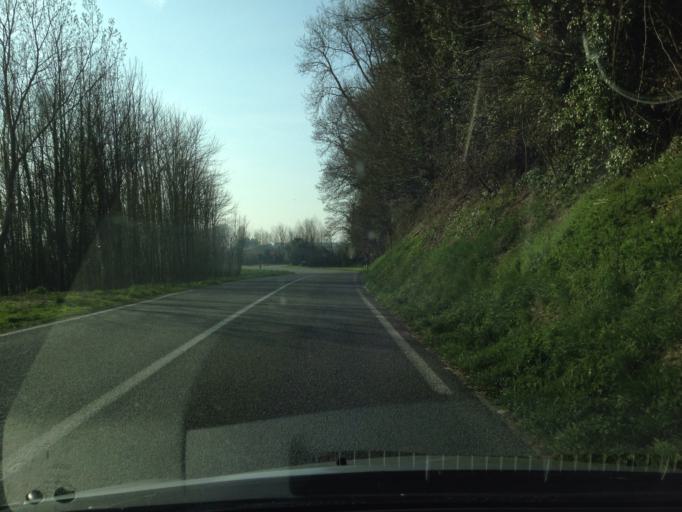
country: FR
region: Nord-Pas-de-Calais
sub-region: Departement du Pas-de-Calais
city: Saint-Josse
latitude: 50.5059
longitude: 1.6708
